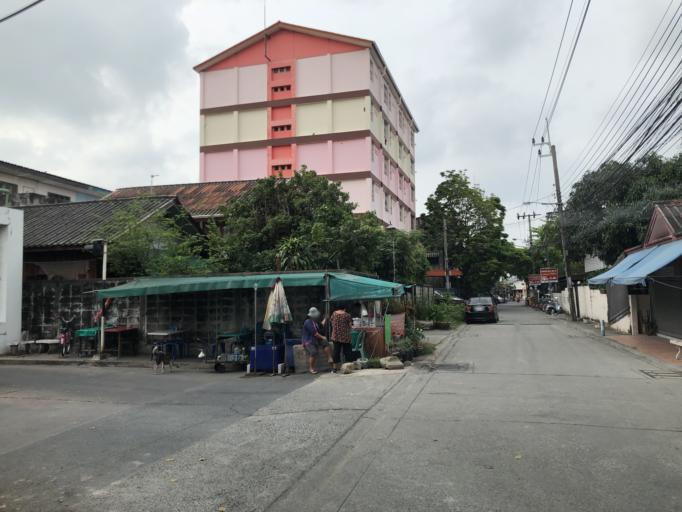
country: TH
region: Bangkok
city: Bang Na
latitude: 13.6043
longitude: 100.6815
